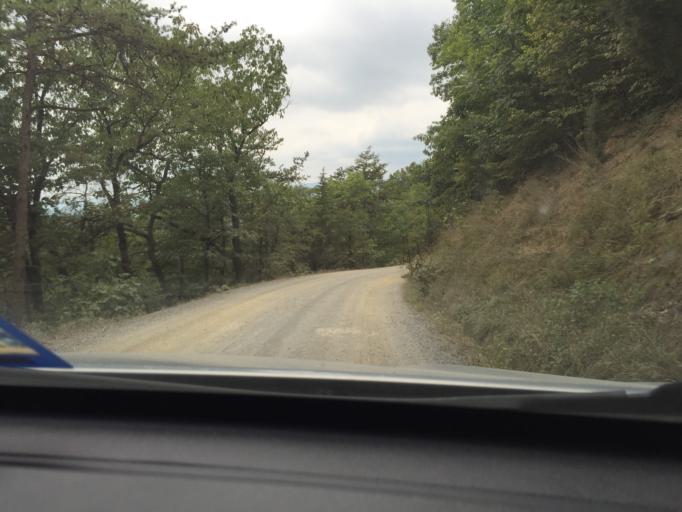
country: US
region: Virginia
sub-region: Shenandoah County
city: Woodstock
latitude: 38.8747
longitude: -78.4607
